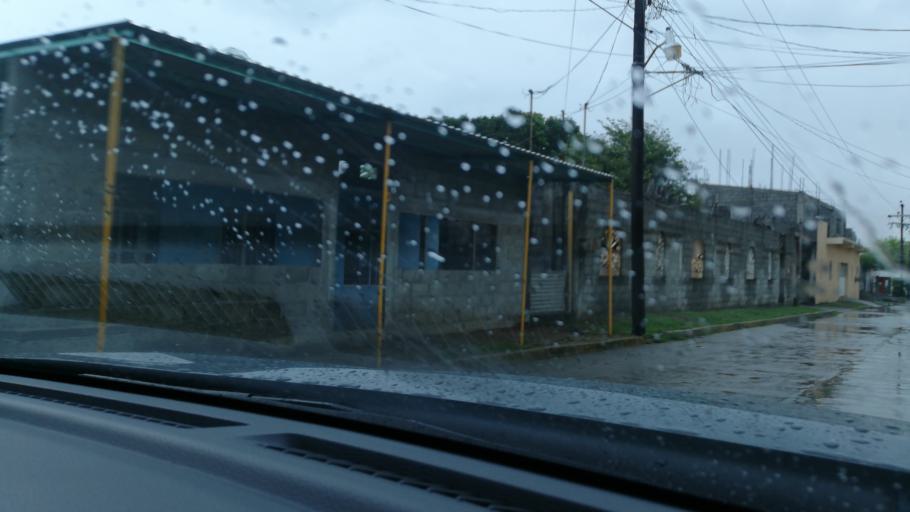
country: MX
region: Oaxaca
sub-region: Salina Cruz
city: Salina Cruz
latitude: 16.2054
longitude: -95.1951
